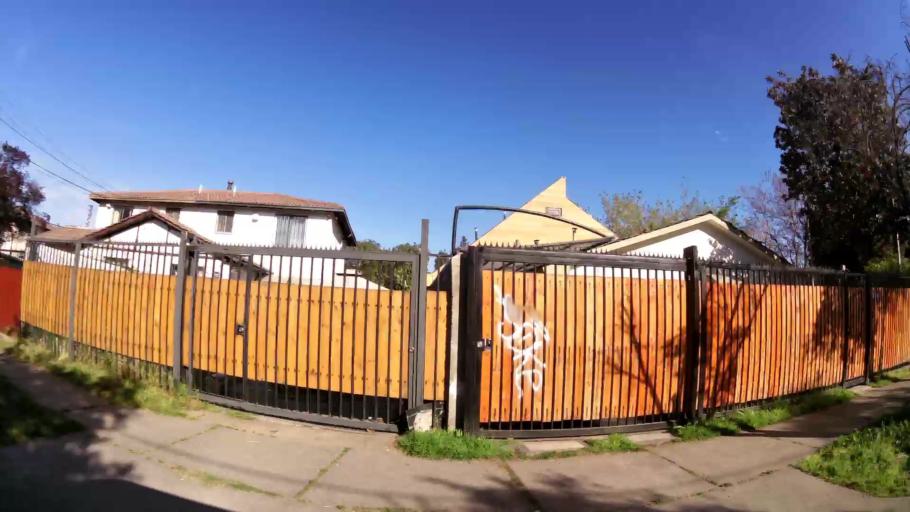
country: CL
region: Santiago Metropolitan
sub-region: Provincia de Santiago
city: Villa Presidente Frei, Nunoa, Santiago, Chile
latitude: -33.4590
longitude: -70.5597
